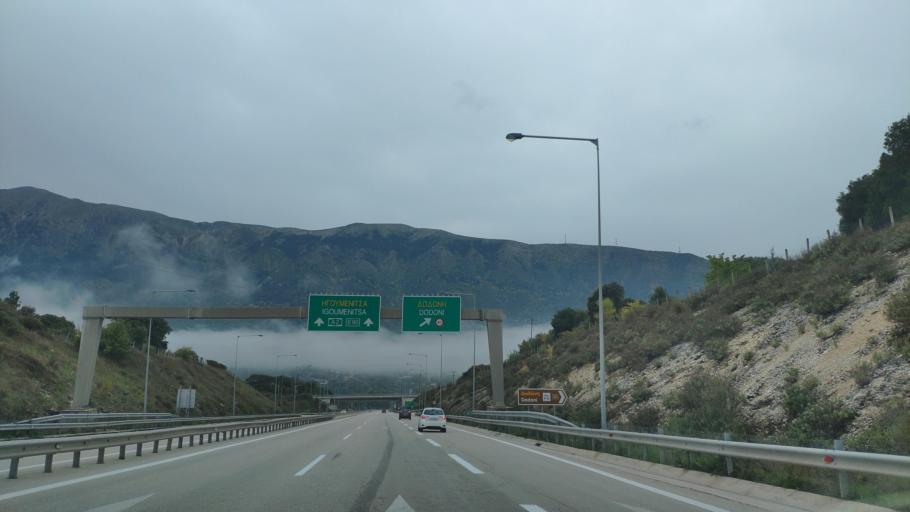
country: GR
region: Epirus
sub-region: Nomos Ioanninon
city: Pedini
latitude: 39.5639
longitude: 20.7779
